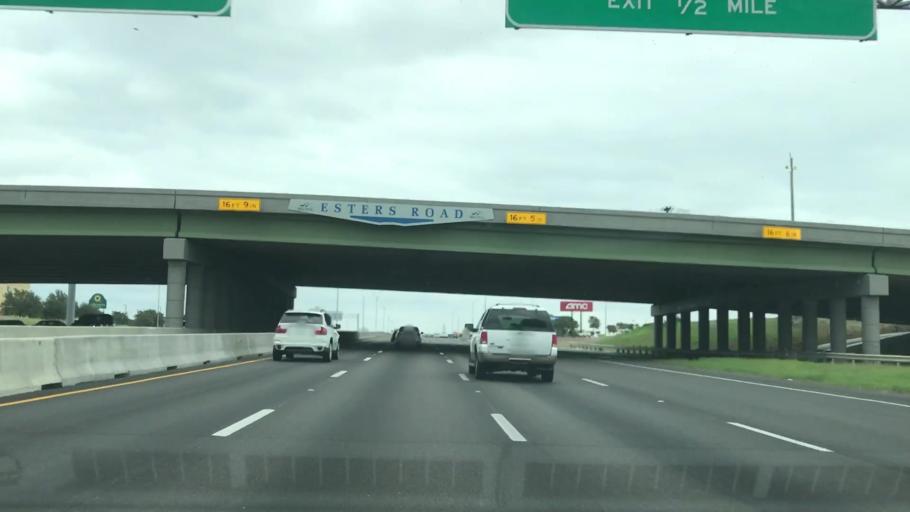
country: US
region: Texas
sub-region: Dallas County
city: Irving
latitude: 32.8370
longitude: -97.0104
